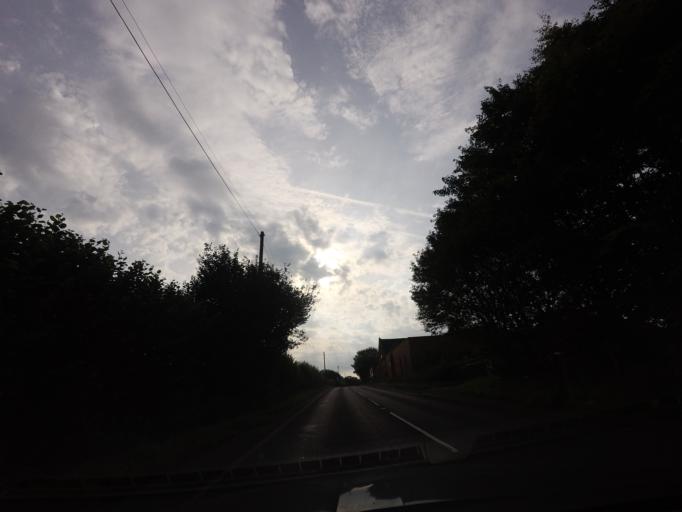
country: GB
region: England
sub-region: Staffordshire
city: Penkridge
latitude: 52.6938
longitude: -2.1367
